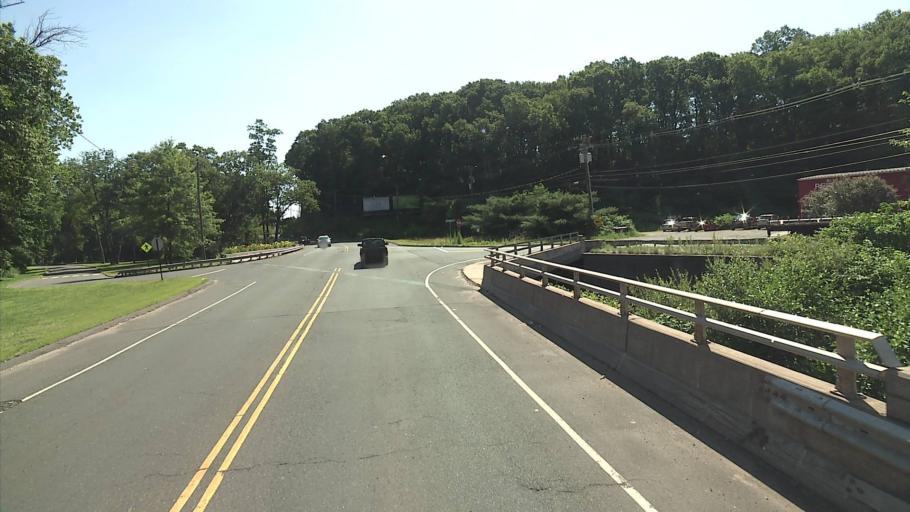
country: US
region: Connecticut
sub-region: Hartford County
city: Bristol
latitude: 41.6705
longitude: -72.9692
